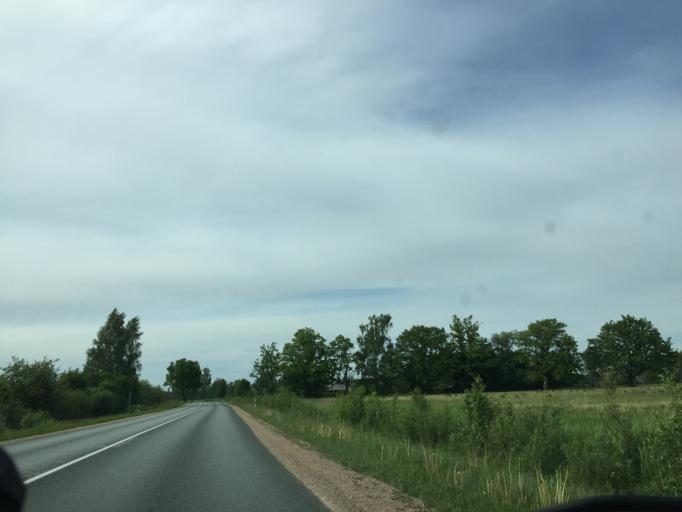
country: LV
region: Beverina
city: Murmuiza
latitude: 57.4534
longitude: 25.4232
